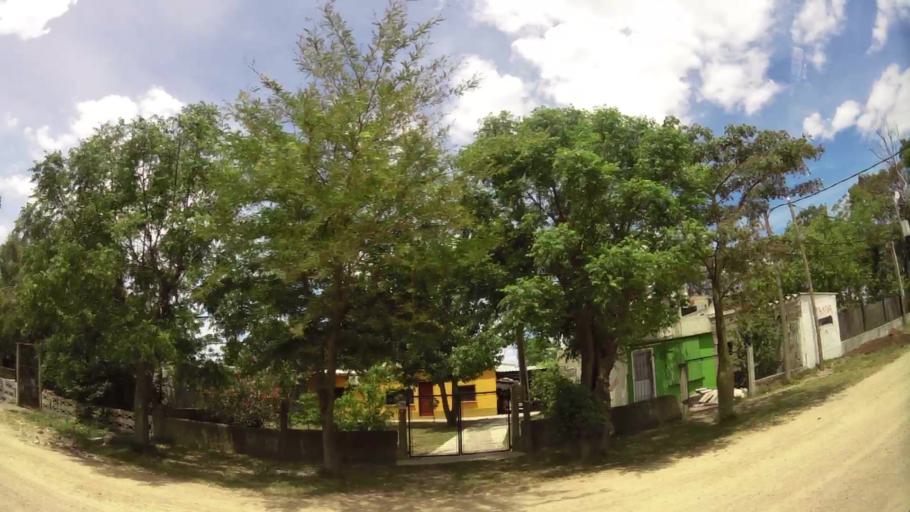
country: UY
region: San Jose
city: Delta del Tigre
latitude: -34.7746
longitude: -56.3761
